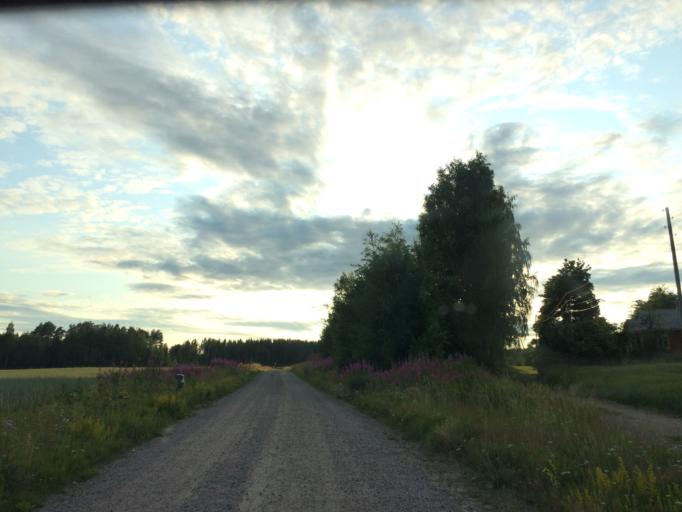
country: FI
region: Haeme
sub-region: Haemeenlinna
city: Janakkala
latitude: 60.8879
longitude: 24.6211
